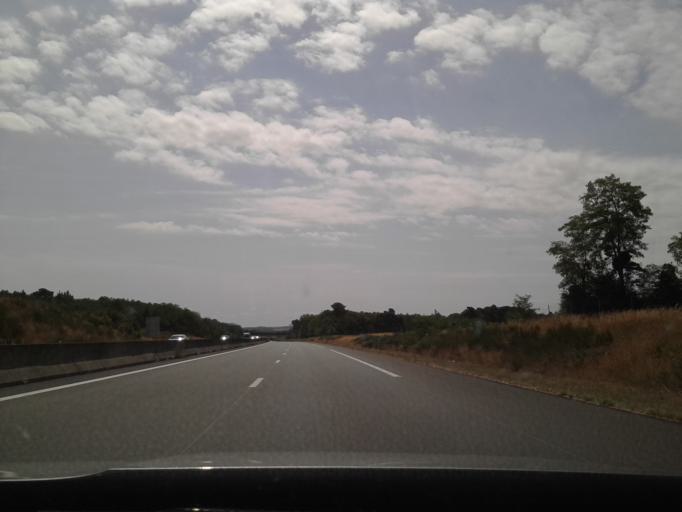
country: FR
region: Pays de la Loire
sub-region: Departement de la Sarthe
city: Luceau
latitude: 47.7044
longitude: 0.3508
